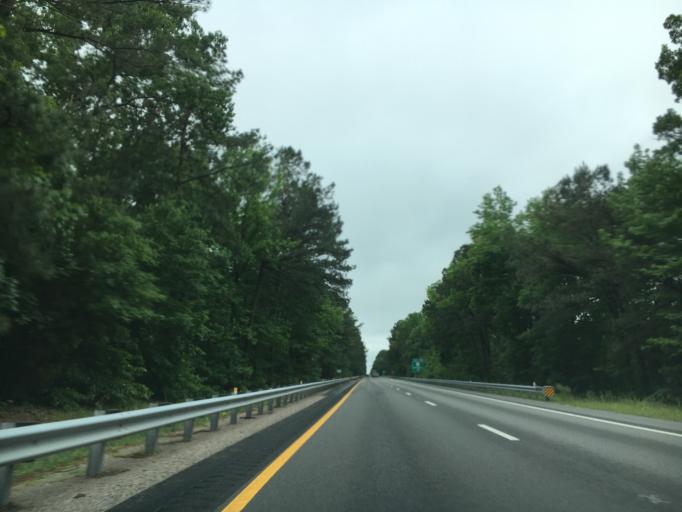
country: US
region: Virginia
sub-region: Dinwiddie County
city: Dinwiddie
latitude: 37.0412
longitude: -77.6243
